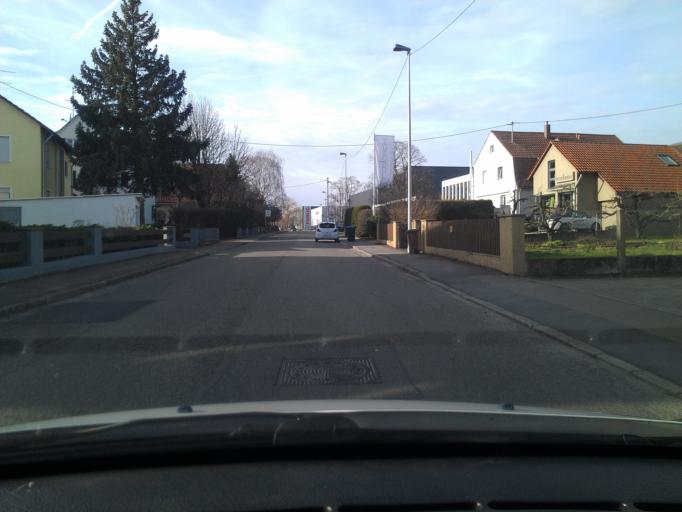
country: DE
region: Baden-Wuerttemberg
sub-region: Regierungsbezirk Stuttgart
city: Neuhausen auf den Fildern
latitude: 48.6841
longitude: 9.2700
